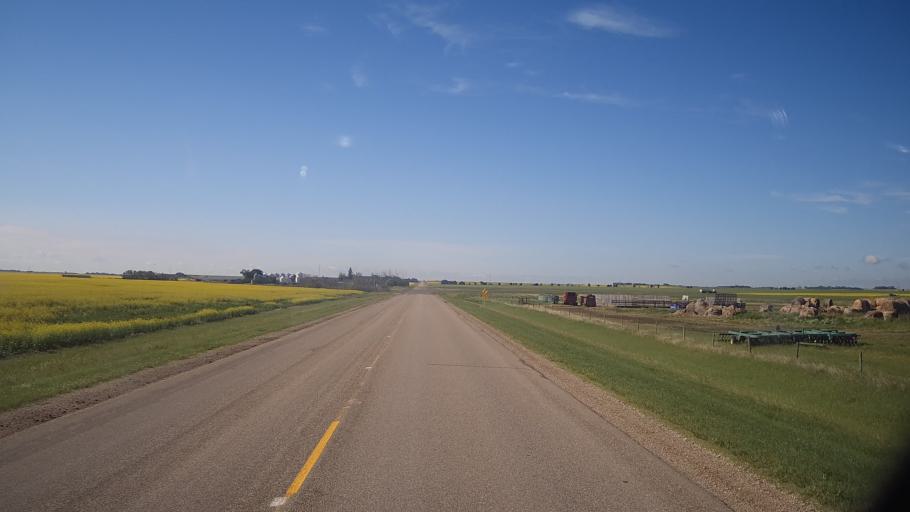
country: CA
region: Saskatchewan
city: Watrous
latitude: 51.6838
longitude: -105.3809
